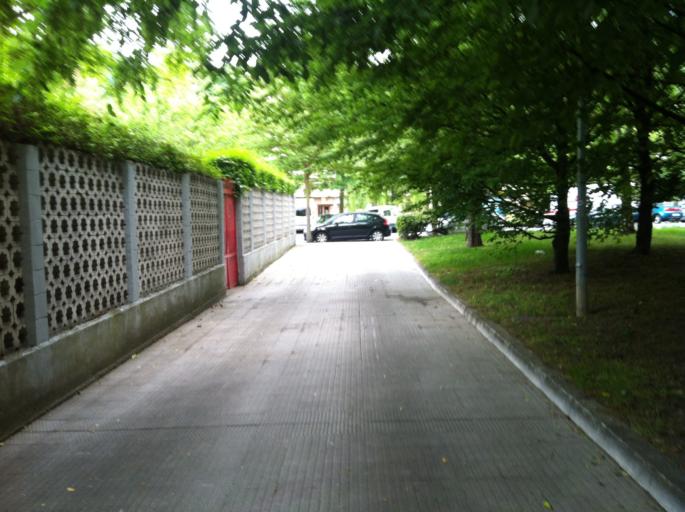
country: ES
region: Basque Country
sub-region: Provincia de Alava
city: Gasteiz / Vitoria
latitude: 42.8524
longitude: -2.6848
